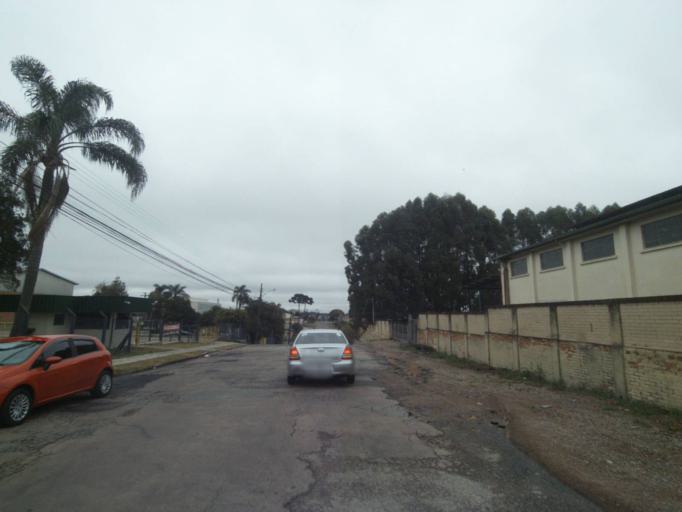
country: BR
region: Parana
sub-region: Curitiba
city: Curitiba
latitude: -25.4989
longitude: -49.3065
